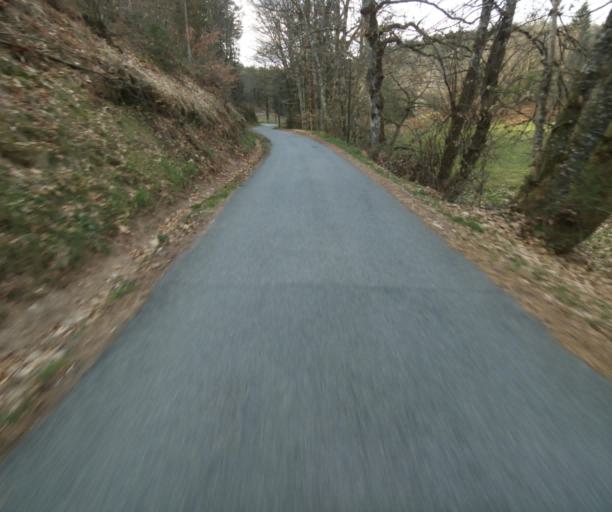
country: FR
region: Limousin
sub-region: Departement de la Correze
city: Correze
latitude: 45.3814
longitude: 1.8591
